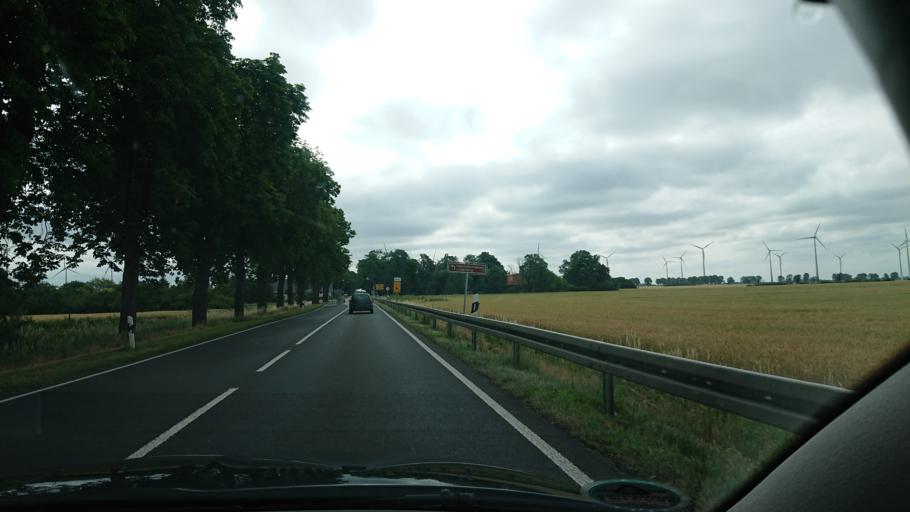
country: DE
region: Brandenburg
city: Plattenburg
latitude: 52.9973
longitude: 12.0826
